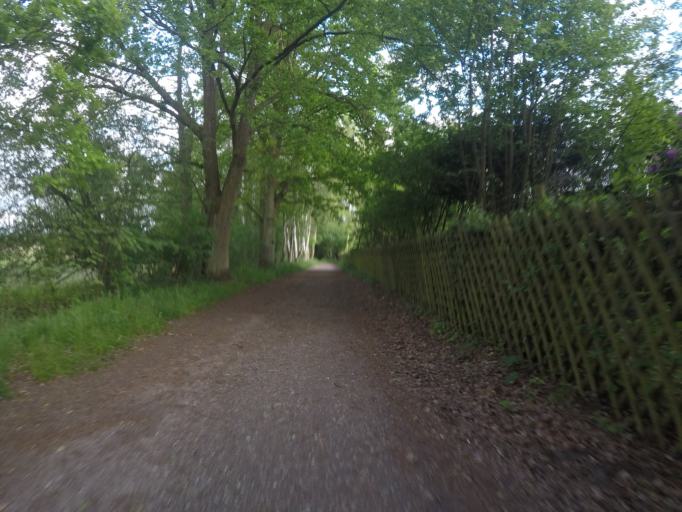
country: DE
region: Schleswig-Holstein
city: Bonningstedt
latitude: 53.6781
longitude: 9.9301
